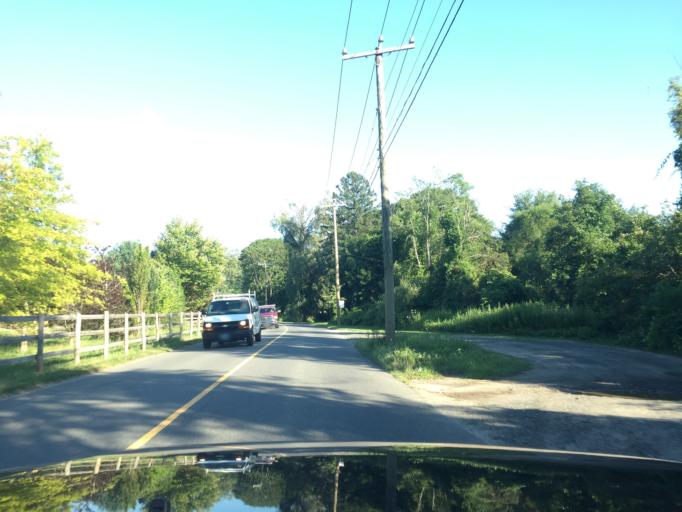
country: US
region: Connecticut
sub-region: Fairfield County
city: Bethel
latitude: 41.3874
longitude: -73.4003
